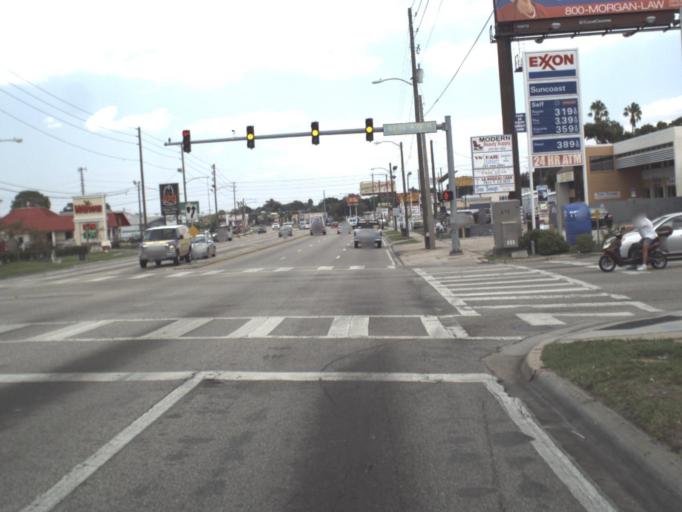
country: US
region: Florida
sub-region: Pinellas County
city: Lealman
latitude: 27.8281
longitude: -82.6795
